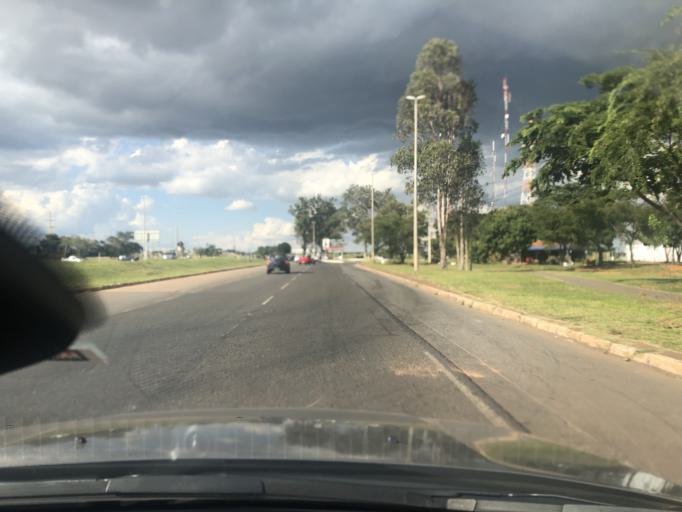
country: BR
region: Federal District
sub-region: Brasilia
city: Brasilia
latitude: -15.9957
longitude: -48.0542
